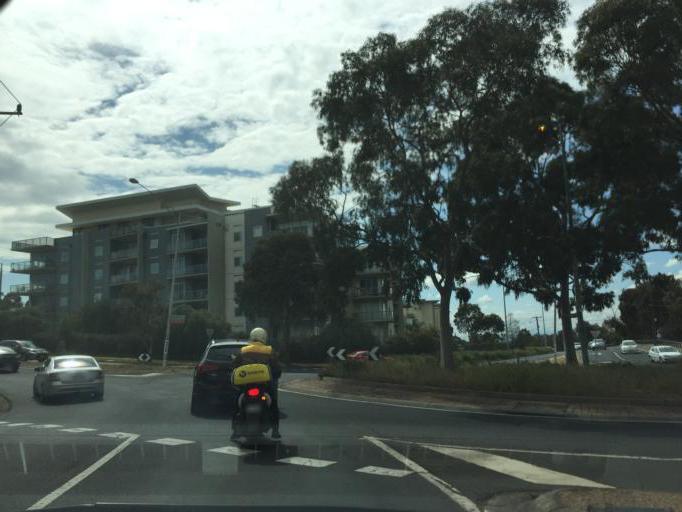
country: AU
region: Victoria
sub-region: Maribyrnong
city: Maribyrnong
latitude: -37.7765
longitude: 144.8907
